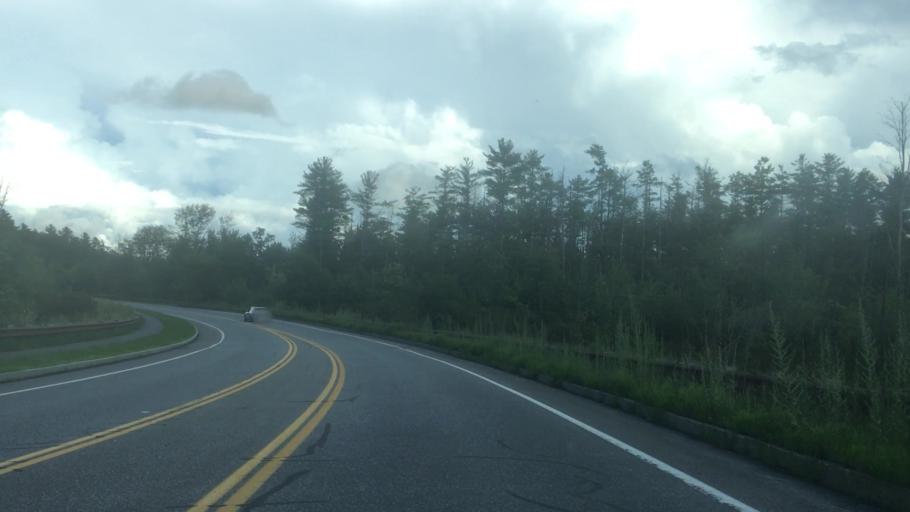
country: US
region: New Hampshire
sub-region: Merrimack County
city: Concord
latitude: 43.1944
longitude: -71.5630
